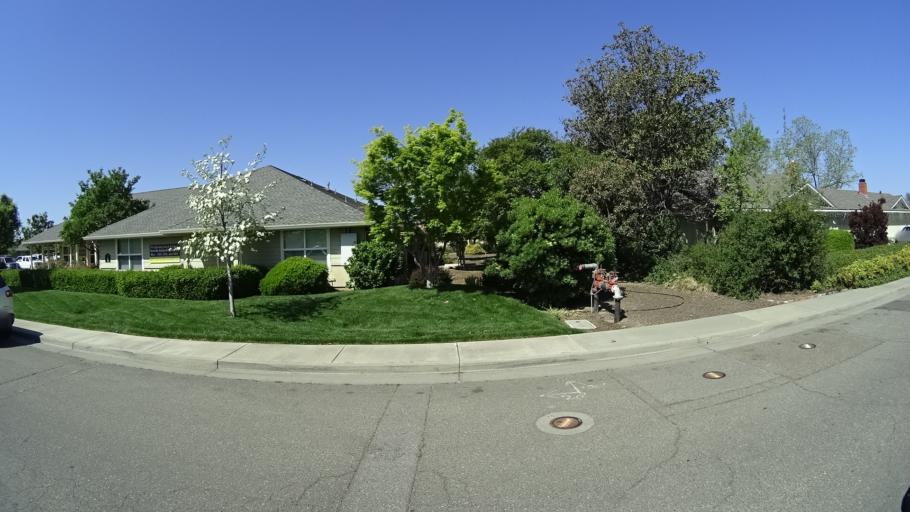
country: US
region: California
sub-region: Glenn County
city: Orland
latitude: 39.7374
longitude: -122.1826
